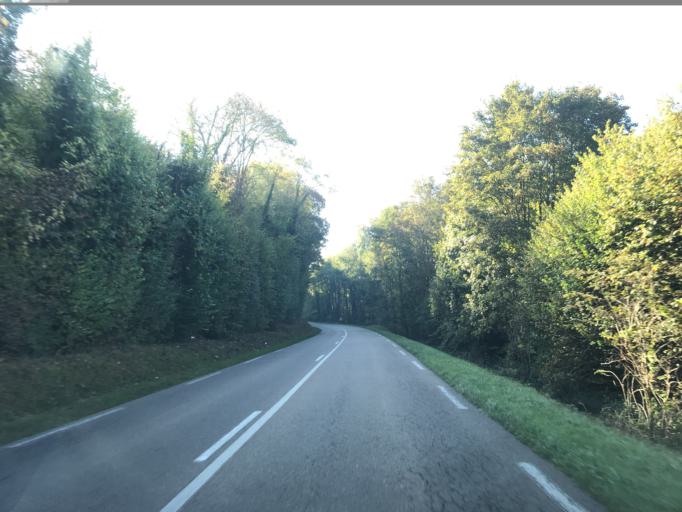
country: FR
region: Haute-Normandie
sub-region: Departement de l'Eure
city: Louviers
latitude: 49.2321
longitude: 1.1851
